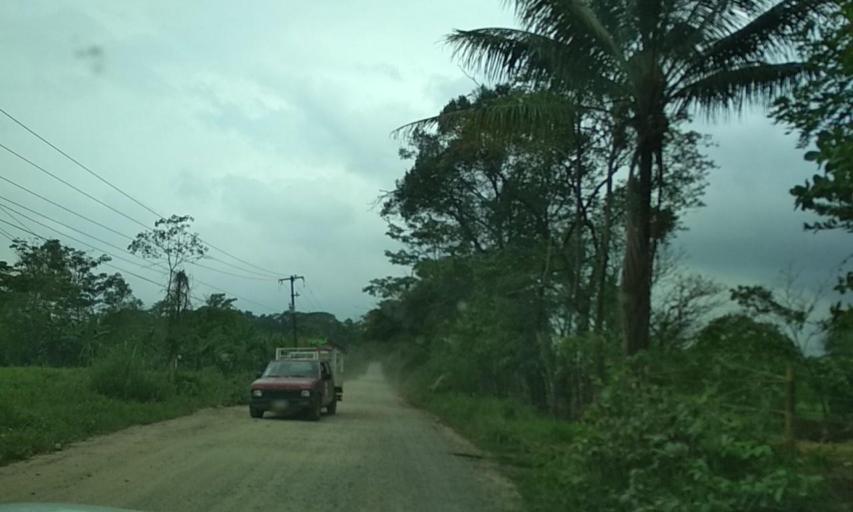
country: MX
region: Veracruz
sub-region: Uxpanapa
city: Poblado 10
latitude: 17.5019
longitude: -94.1511
